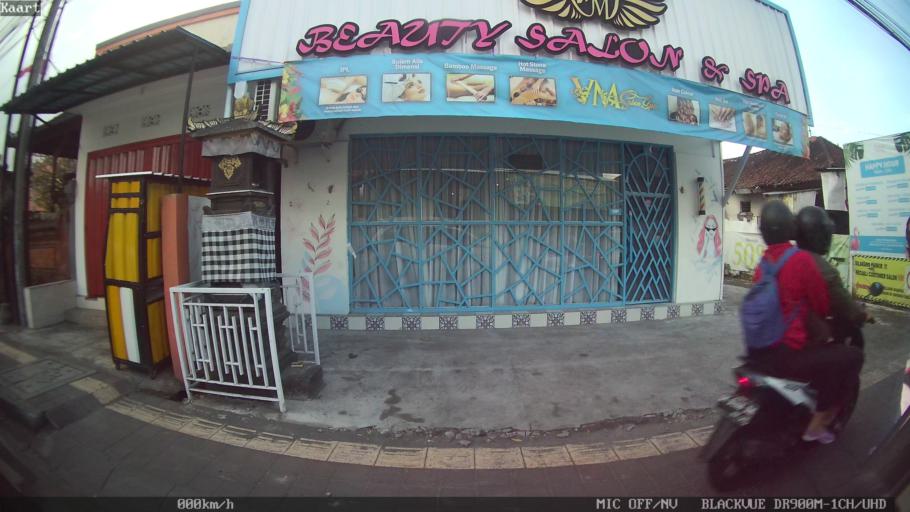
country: ID
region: Bali
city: Karyadharma
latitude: -8.6939
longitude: 115.1976
